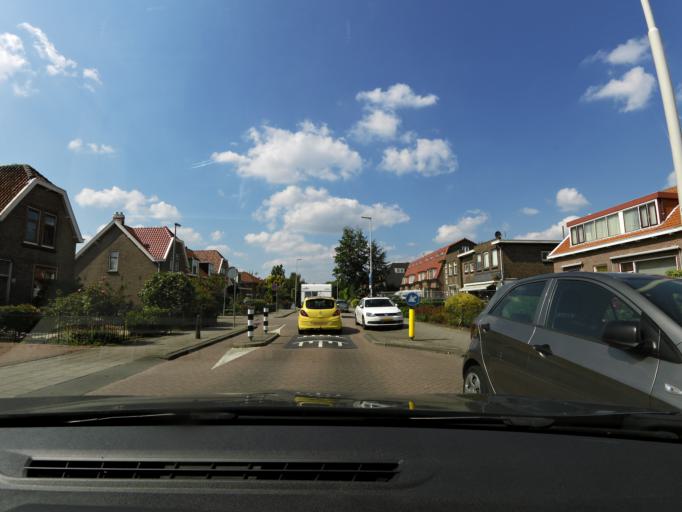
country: NL
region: South Holland
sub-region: Gemeente Schiedam
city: Schiedam
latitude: 51.8889
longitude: 4.3877
